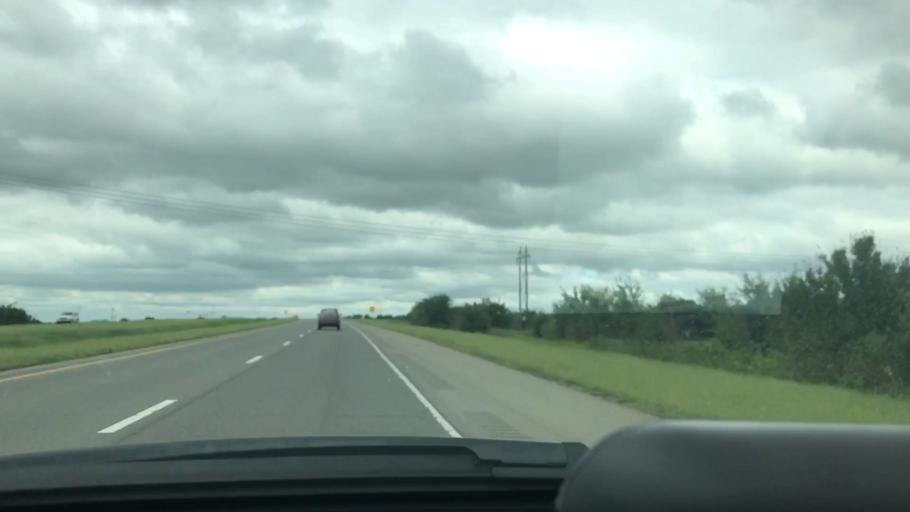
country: US
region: Oklahoma
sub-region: McIntosh County
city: Checotah
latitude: 35.5708
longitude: -95.4910
